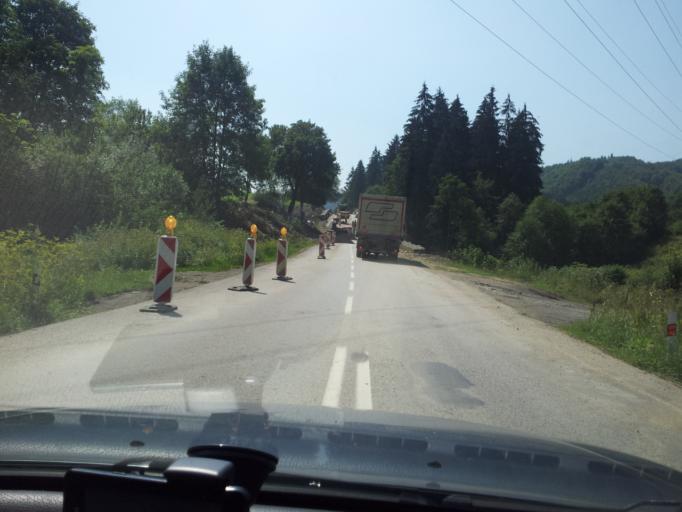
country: SK
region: Zilinsky
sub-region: Okres Dolny Kubin
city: Dolny Kubin
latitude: 49.2811
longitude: 19.3470
